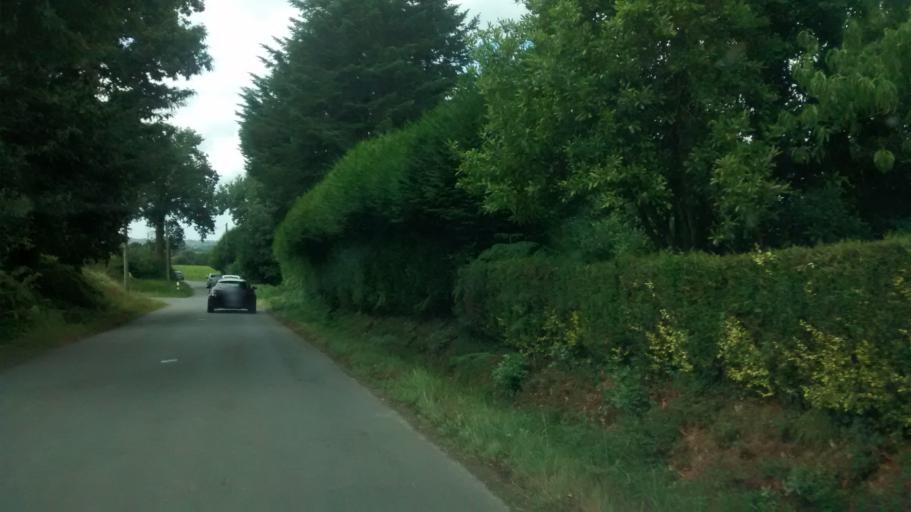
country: FR
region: Brittany
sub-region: Departement d'Ille-et-Vilaine
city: Hede-Bazouges
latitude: 48.2917
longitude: -1.8292
